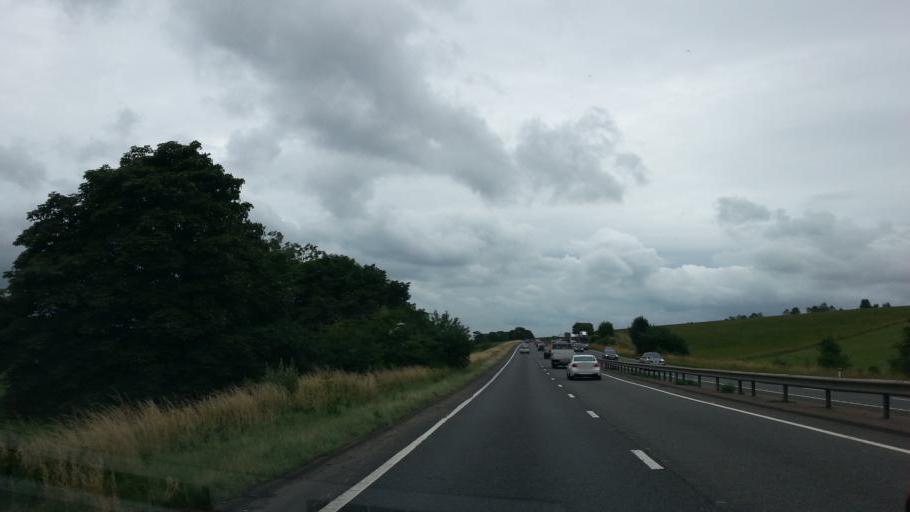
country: GB
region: England
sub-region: Oxfordshire
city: Harwell
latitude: 51.5358
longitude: -1.2939
